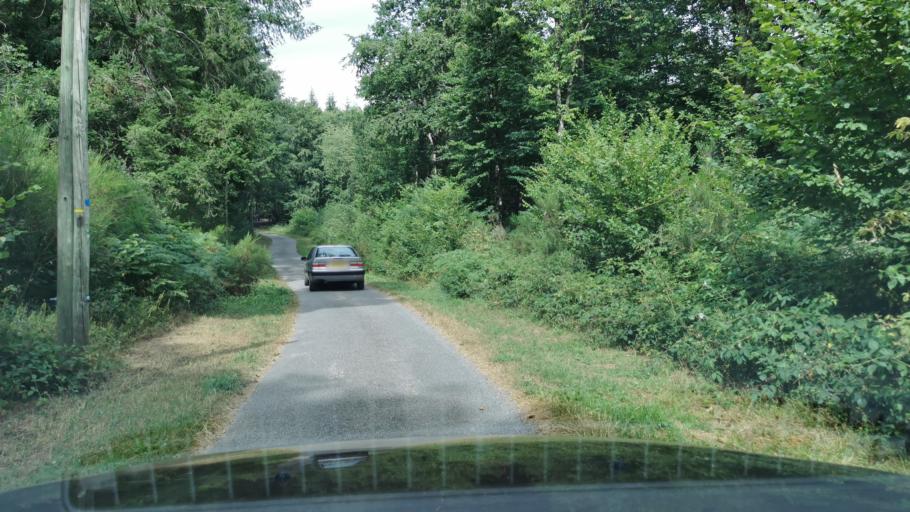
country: FR
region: Bourgogne
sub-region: Departement de Saone-et-Loire
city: Marmagne
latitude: 46.8022
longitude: 4.2717
